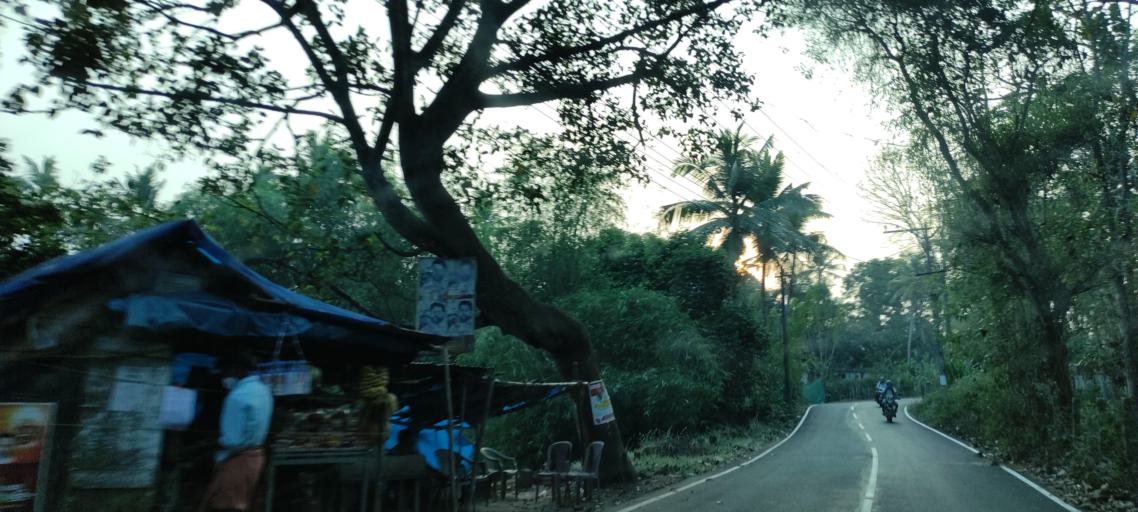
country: IN
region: Kerala
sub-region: Alappuzha
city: Mavelikara
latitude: 9.2700
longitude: 76.5514
